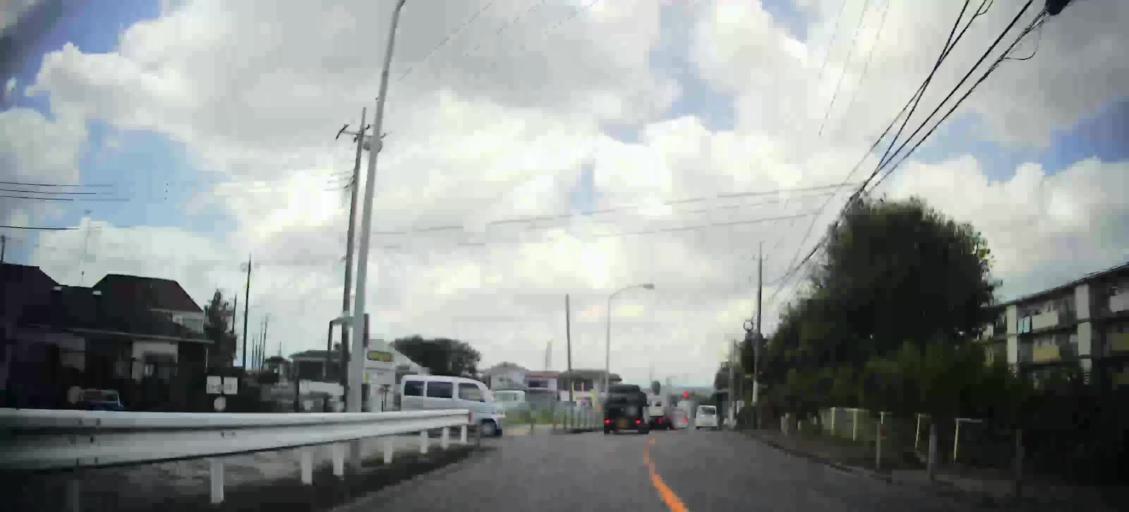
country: JP
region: Kanagawa
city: Yokohama
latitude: 35.4688
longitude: 139.5585
